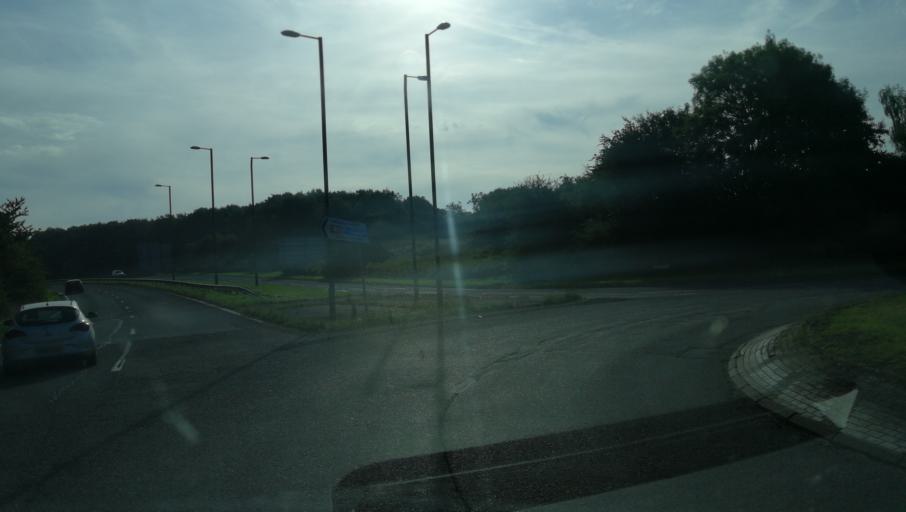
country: GB
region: England
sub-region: Oxfordshire
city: Yarnton
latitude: 51.7970
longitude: -1.2874
